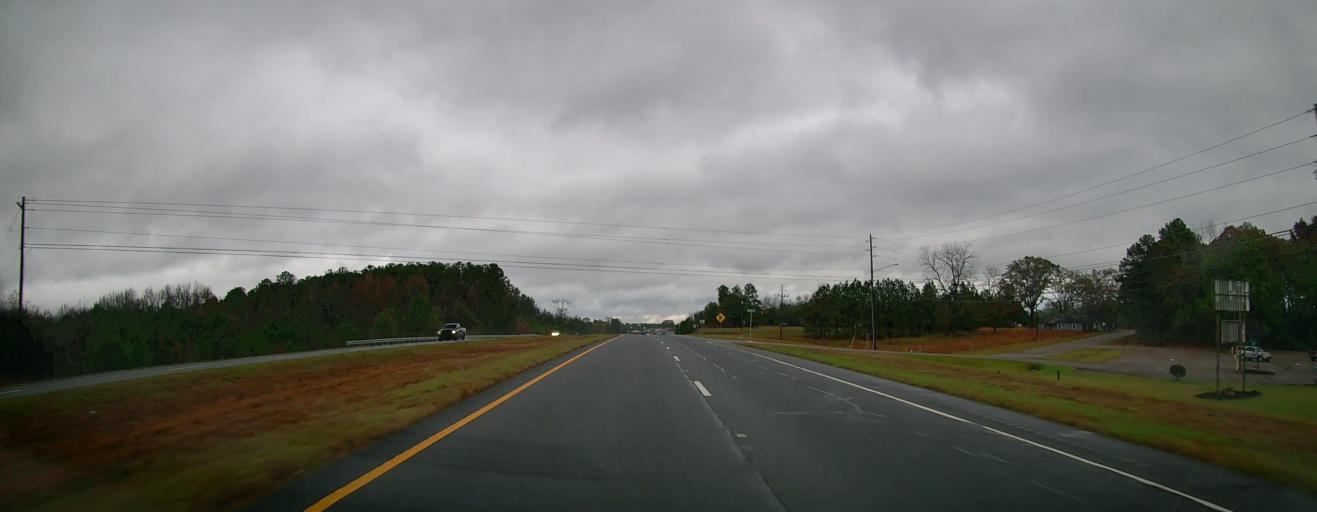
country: US
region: Georgia
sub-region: Jackson County
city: Commerce
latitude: 34.1722
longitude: -83.4449
